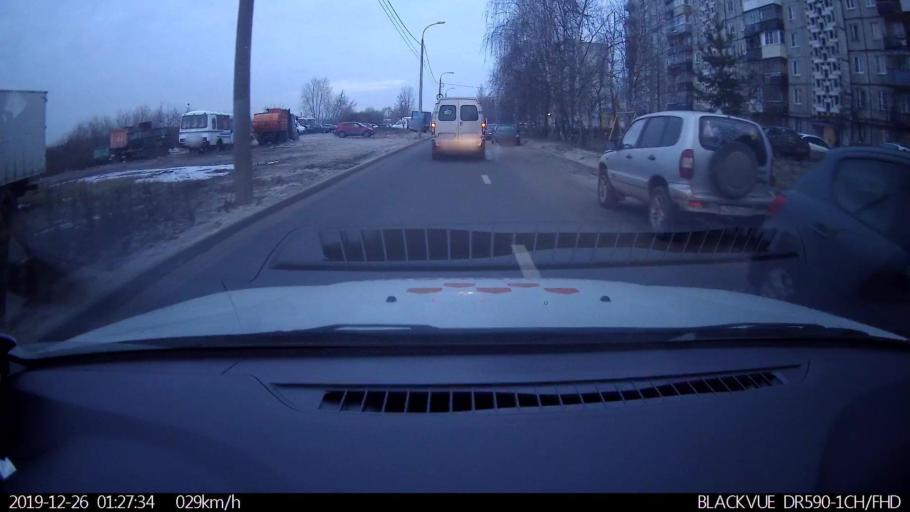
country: RU
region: Nizjnij Novgorod
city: Gorbatovka
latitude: 56.2725
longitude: 43.8772
